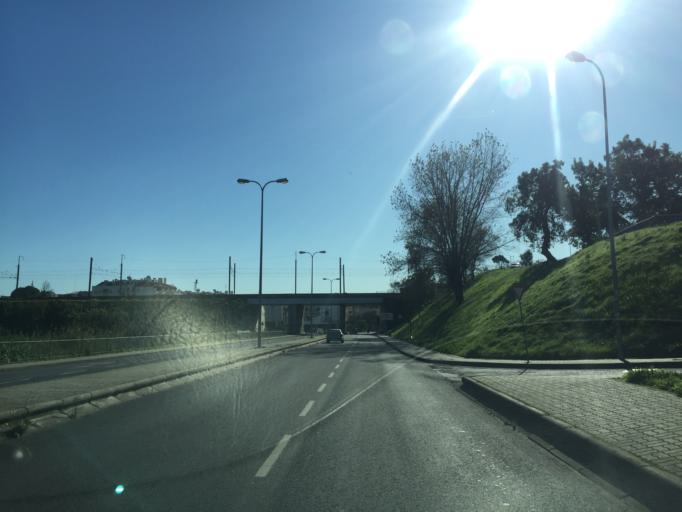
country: PT
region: Lisbon
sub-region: Sintra
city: Queluz
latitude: 38.7620
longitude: -9.2513
